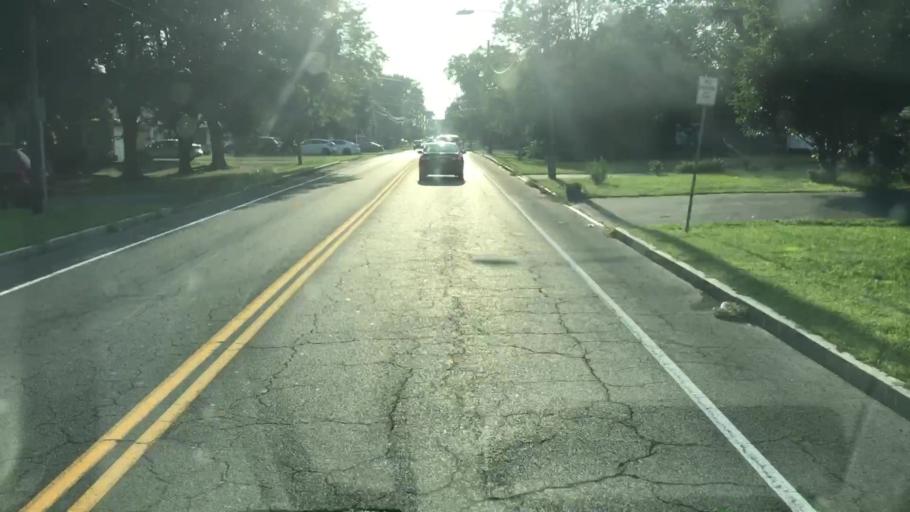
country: US
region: New York
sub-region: Onondaga County
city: Mattydale
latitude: 43.1129
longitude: -76.1479
